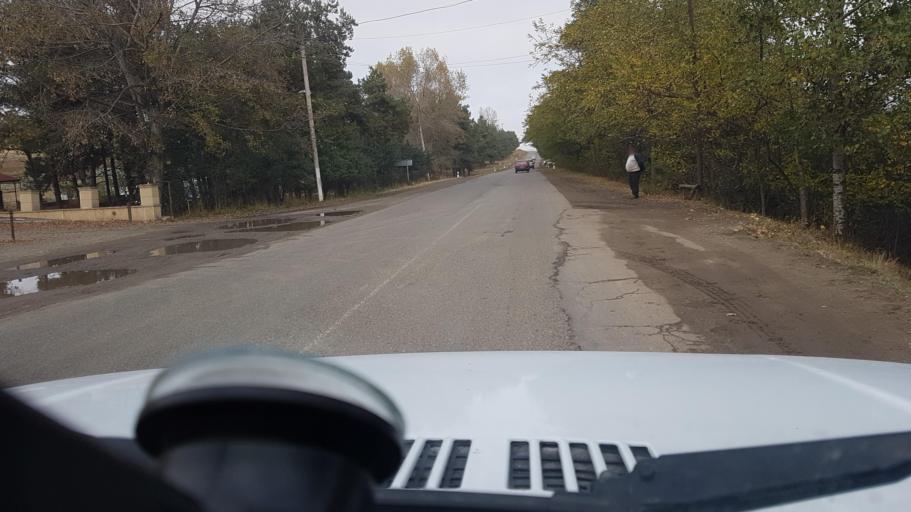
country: AZ
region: Gadabay Rayon
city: Ariqdam
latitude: 40.6343
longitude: 45.8131
